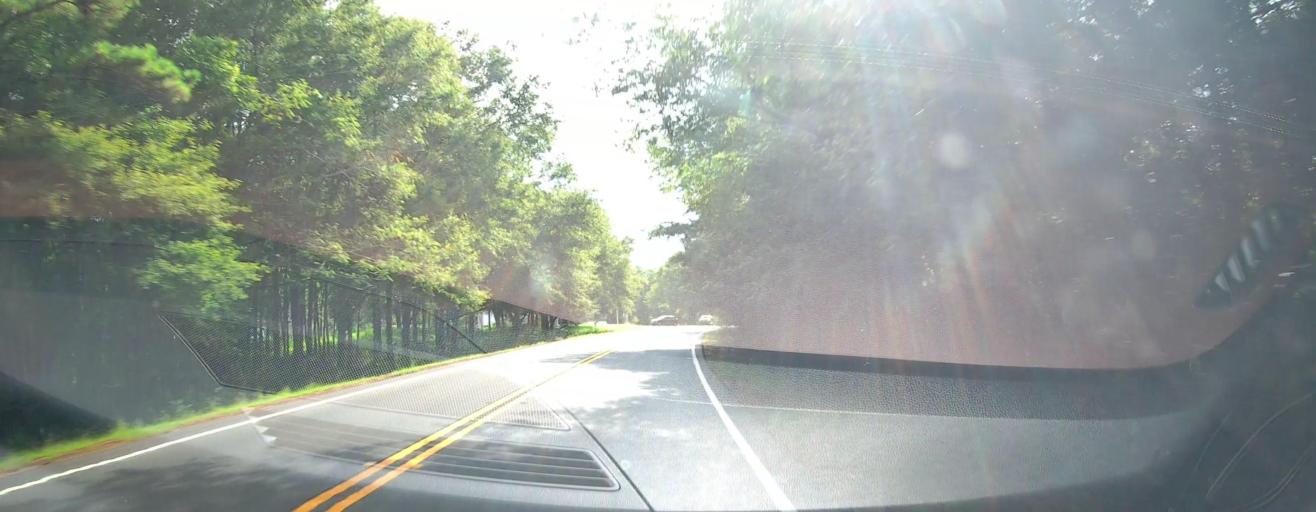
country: US
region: Georgia
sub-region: Meriwether County
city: Manchester
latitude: 32.9881
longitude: -84.5798
